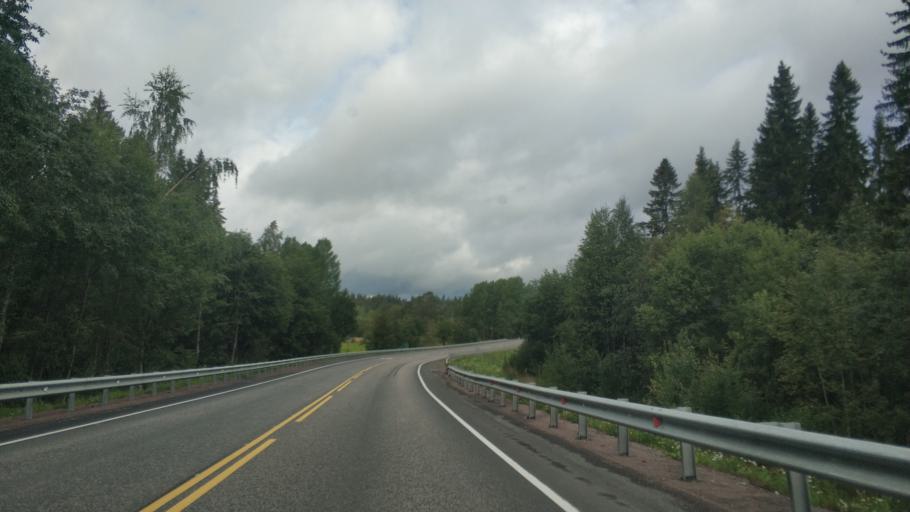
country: RU
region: Republic of Karelia
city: Khelyulya
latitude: 61.7962
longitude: 30.6195
